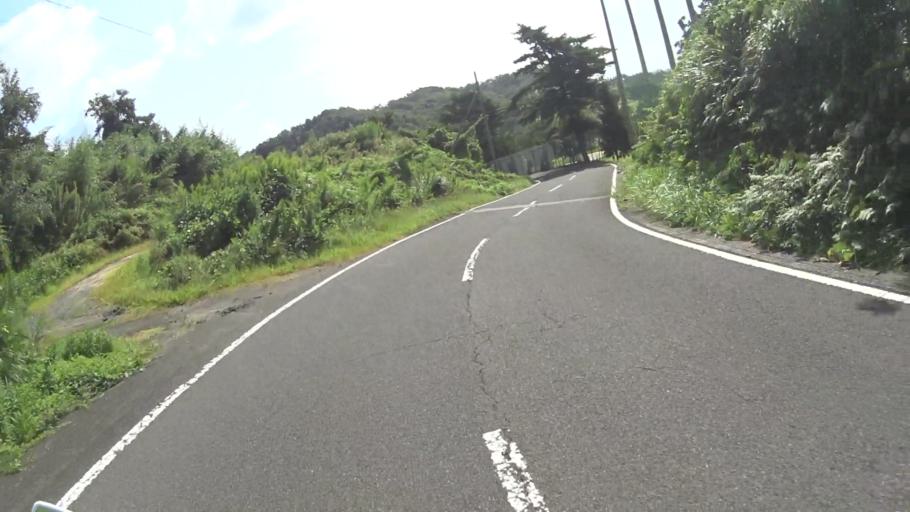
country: JP
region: Kyoto
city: Miyazu
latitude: 35.6277
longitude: 135.2216
